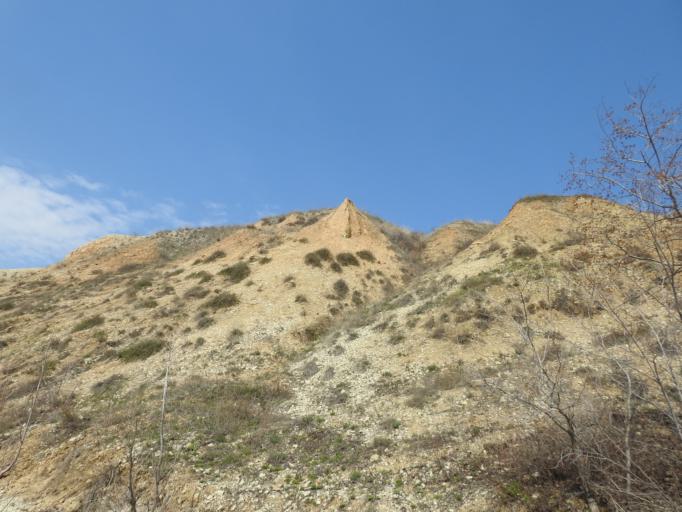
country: RU
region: Saratov
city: Voskresenskoye
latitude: 51.7968
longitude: 46.8860
